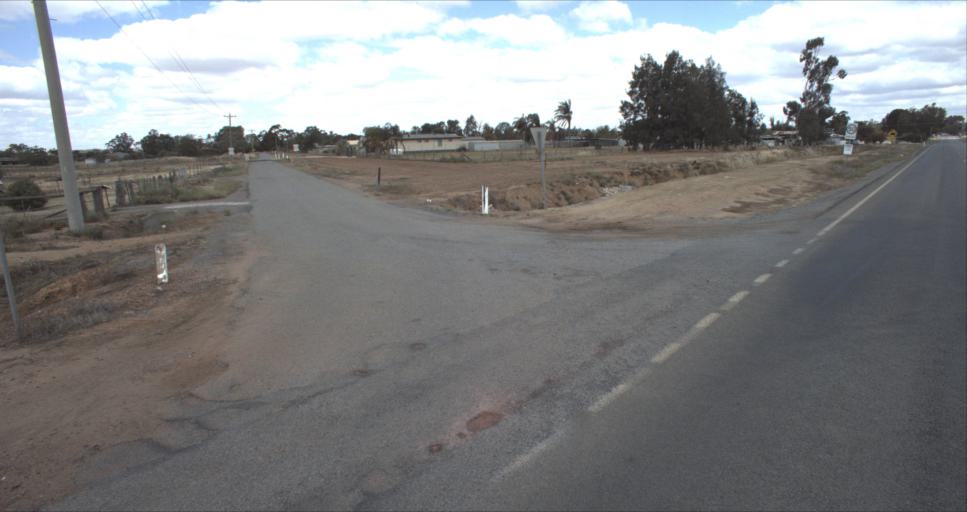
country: AU
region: New South Wales
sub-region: Leeton
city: Leeton
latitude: -34.5955
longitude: 146.4054
